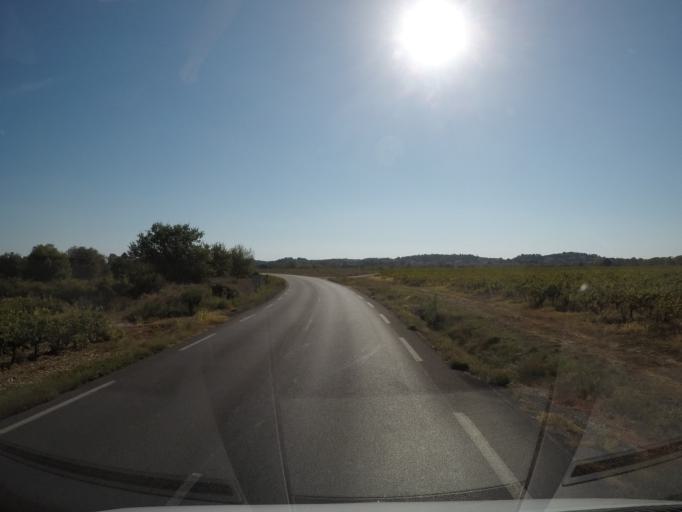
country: FR
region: Languedoc-Roussillon
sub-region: Departement du Gard
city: Lezan
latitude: 44.0224
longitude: 4.0396
